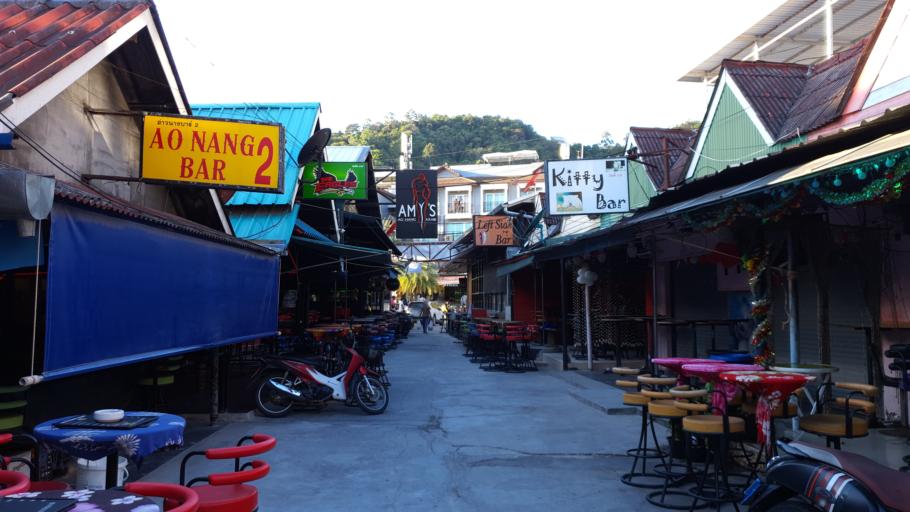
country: TH
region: Phangnga
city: Ban Ao Nang
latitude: 8.0321
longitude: 98.8252
